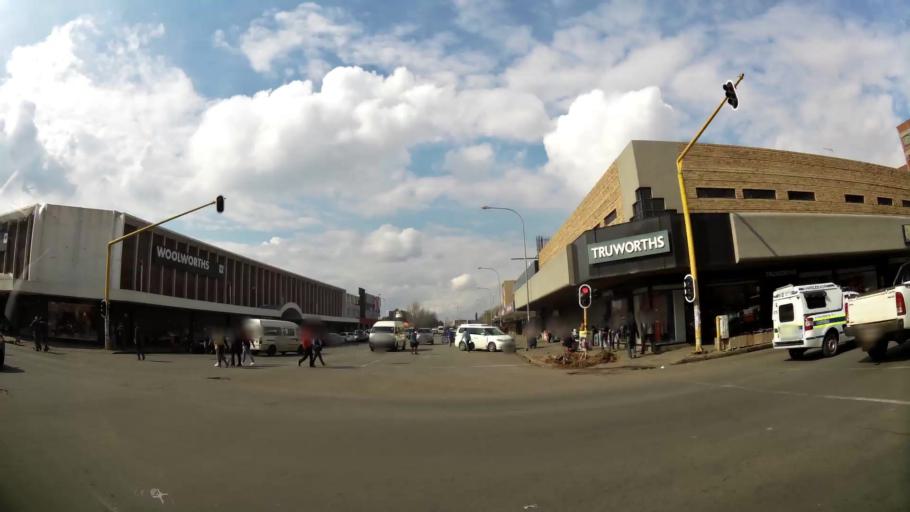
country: ZA
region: Gauteng
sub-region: Sedibeng District Municipality
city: Vereeniging
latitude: -26.6737
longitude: 27.9319
